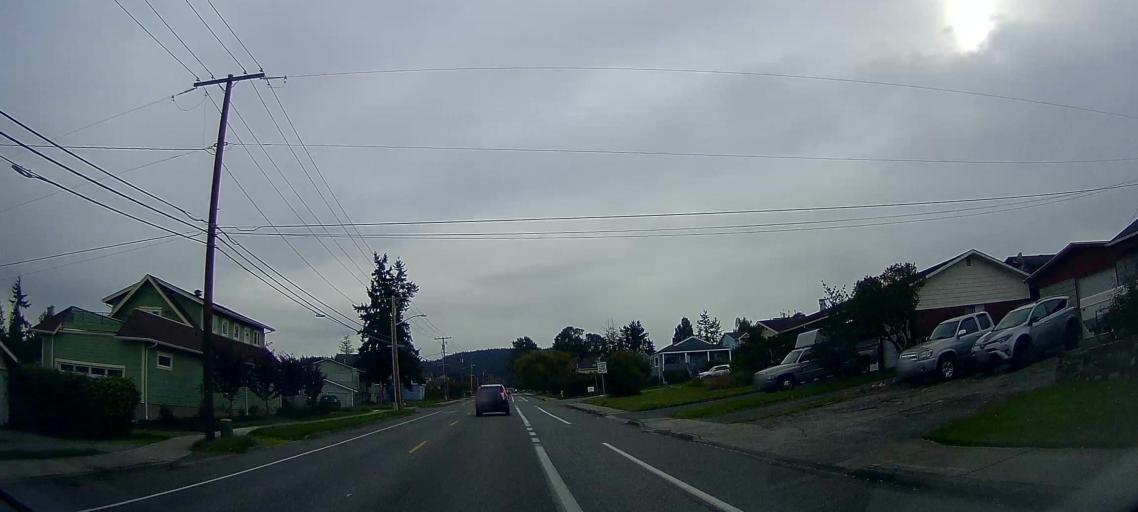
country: US
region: Washington
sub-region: Skagit County
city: Anacortes
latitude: 48.4987
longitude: -122.6176
